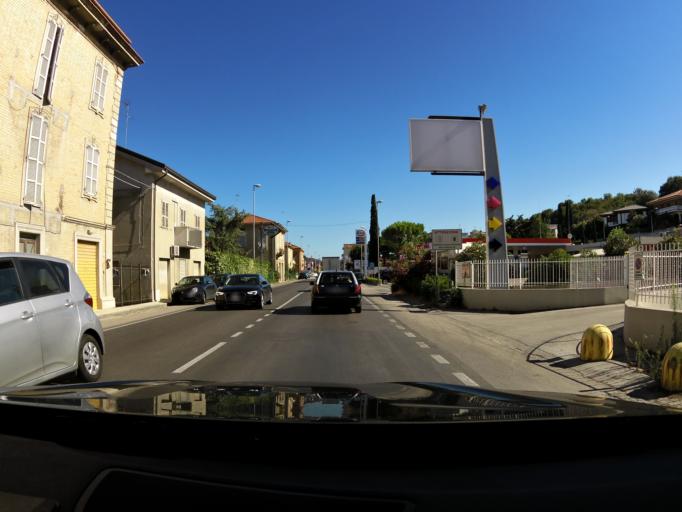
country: IT
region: The Marches
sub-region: Province of Fermo
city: Porto San Giorgio
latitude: 43.1752
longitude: 13.7958
